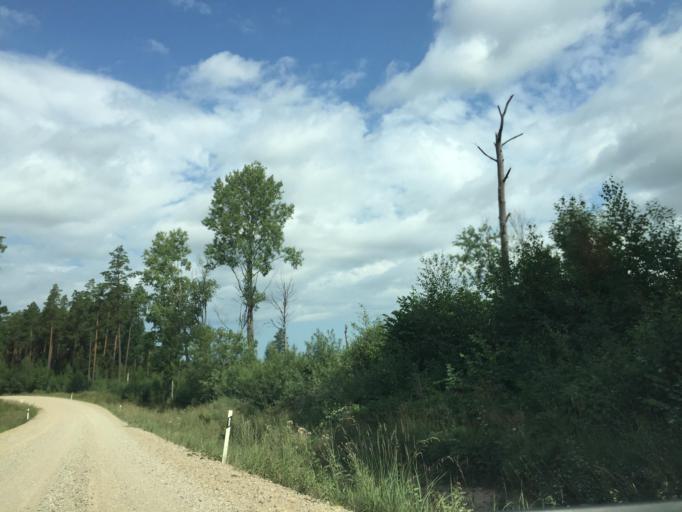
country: LV
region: Kandava
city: Kandava
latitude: 57.0165
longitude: 22.8287
